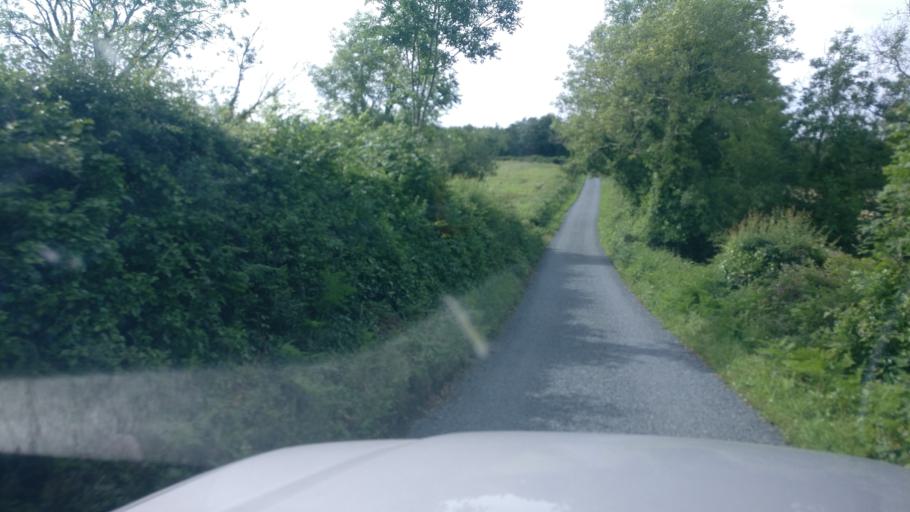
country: IE
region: Connaught
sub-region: County Galway
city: Gort
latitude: 53.1094
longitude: -8.7170
